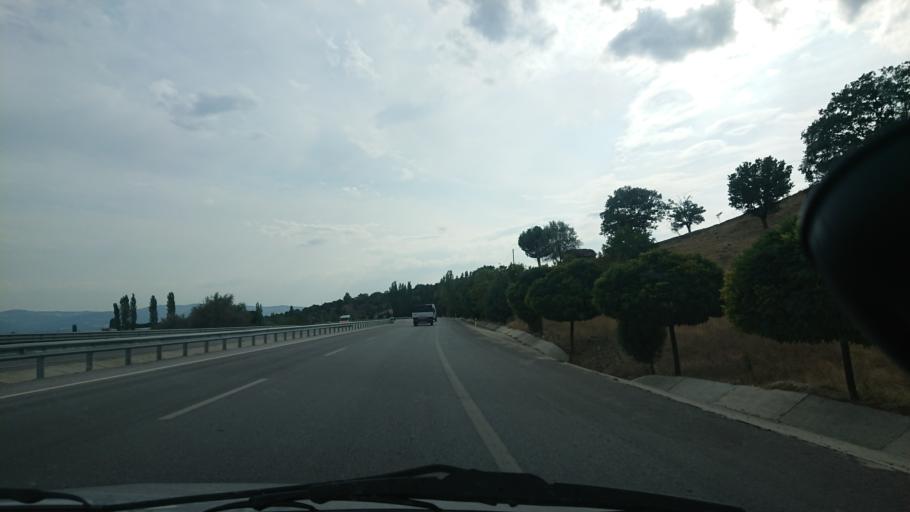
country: TR
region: Kuetahya
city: Gediz
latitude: 39.0169
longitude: 29.4117
